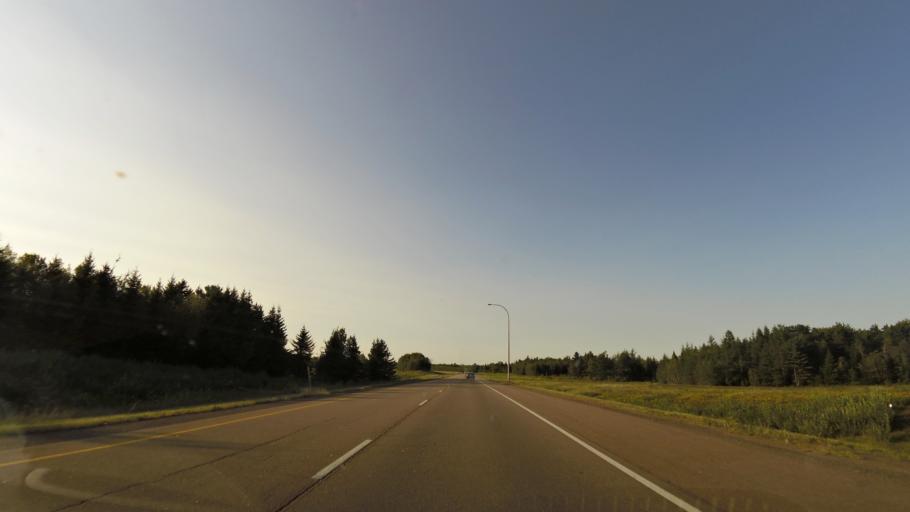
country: CA
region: New Brunswick
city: Dieppe
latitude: 46.1020
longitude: -64.6068
